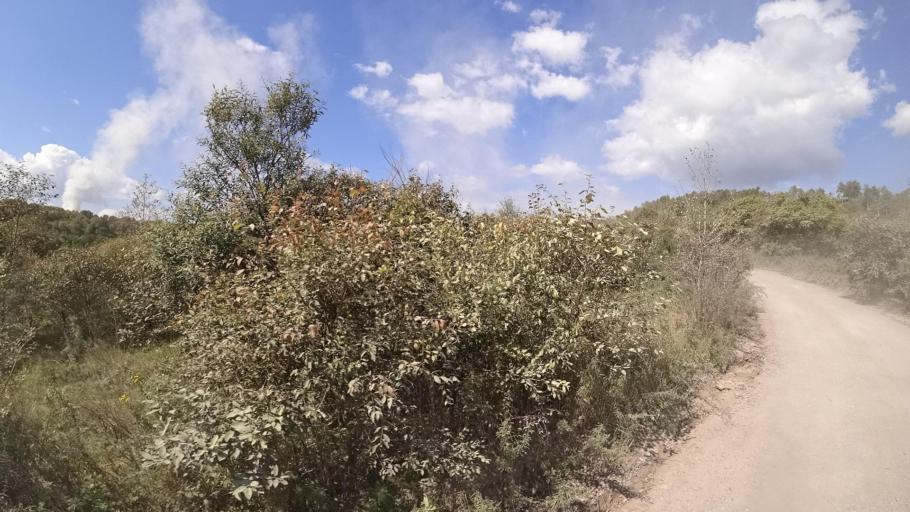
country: RU
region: Jewish Autonomous Oblast
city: Londoko
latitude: 49.0074
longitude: 131.9138
